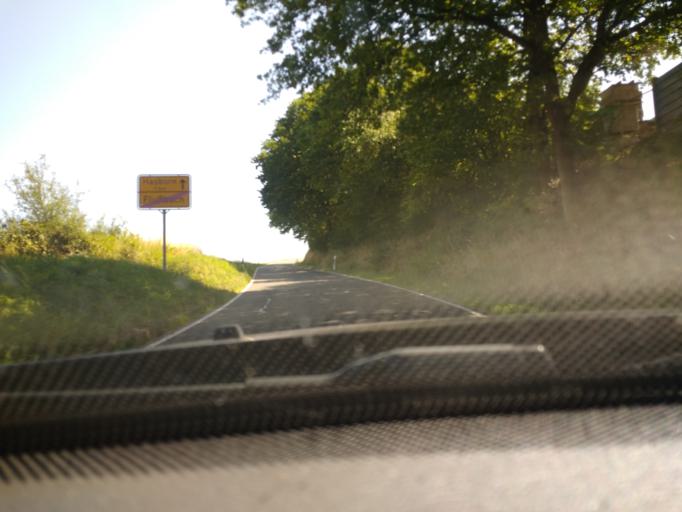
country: DE
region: Rheinland-Pfalz
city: Flussbach
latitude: 50.0159
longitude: 6.9316
